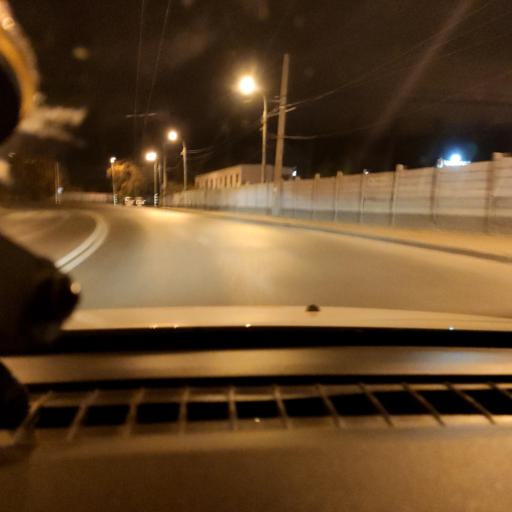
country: RU
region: Samara
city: Rozhdestveno
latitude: 53.1666
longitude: 50.0737
